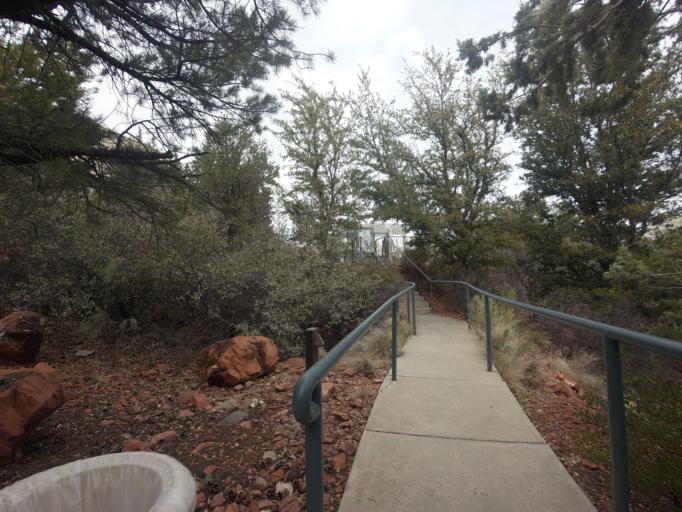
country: US
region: Arizona
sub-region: Yavapai County
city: Big Park
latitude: 34.7712
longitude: -111.7675
